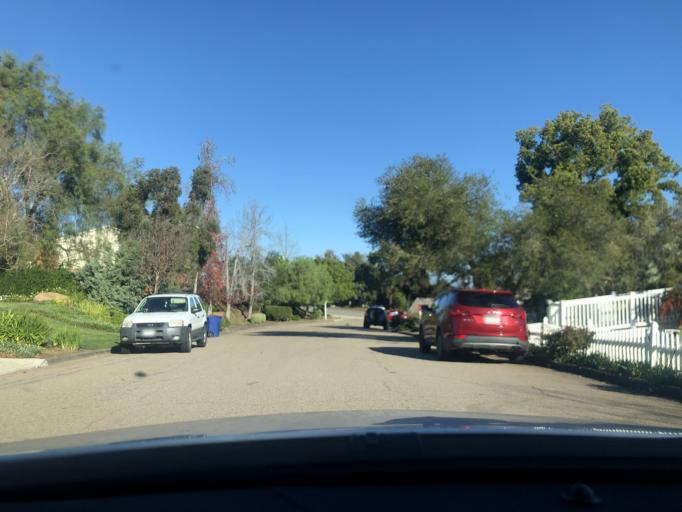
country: US
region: California
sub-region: San Diego County
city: Casa de Oro-Mount Helix
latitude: 32.7690
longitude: -116.9469
